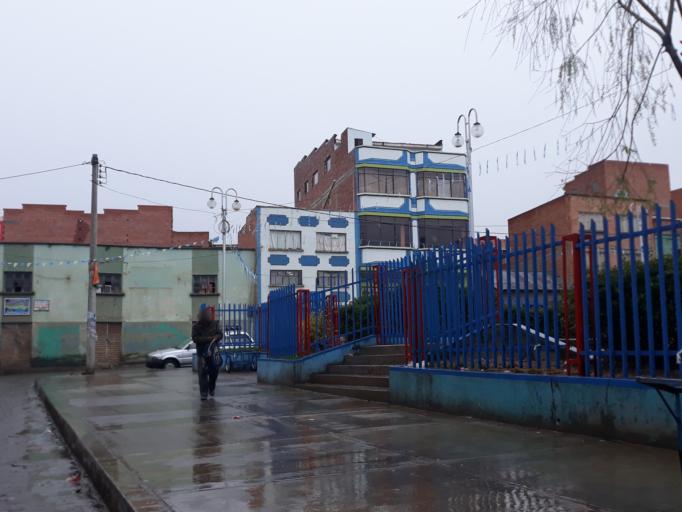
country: BO
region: La Paz
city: Achacachi
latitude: -16.0411
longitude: -68.6854
